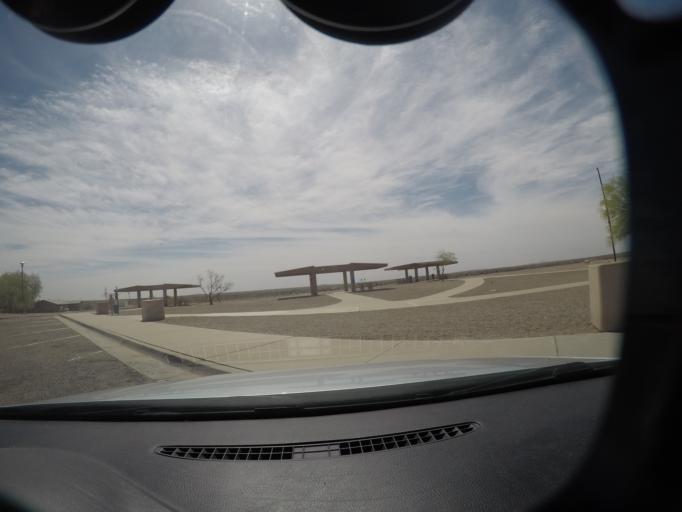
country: US
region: Arizona
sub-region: Maricopa County
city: Gila Bend
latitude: 32.8495
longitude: -113.2648
